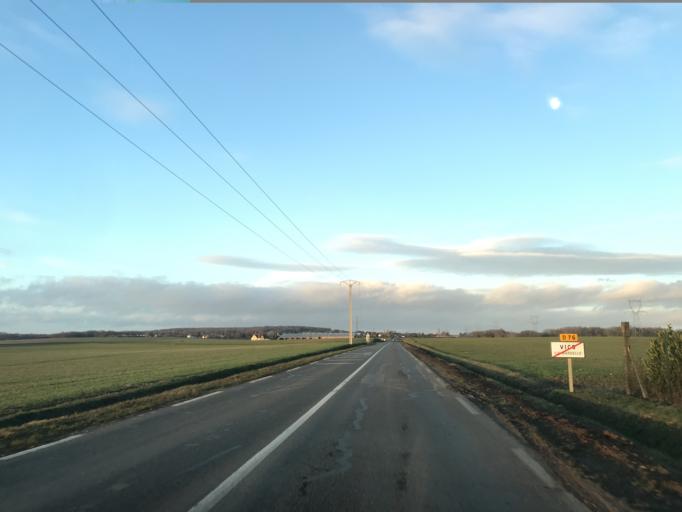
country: FR
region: Ile-de-France
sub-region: Departement des Yvelines
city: Galluis
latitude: 48.8227
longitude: 1.8196
